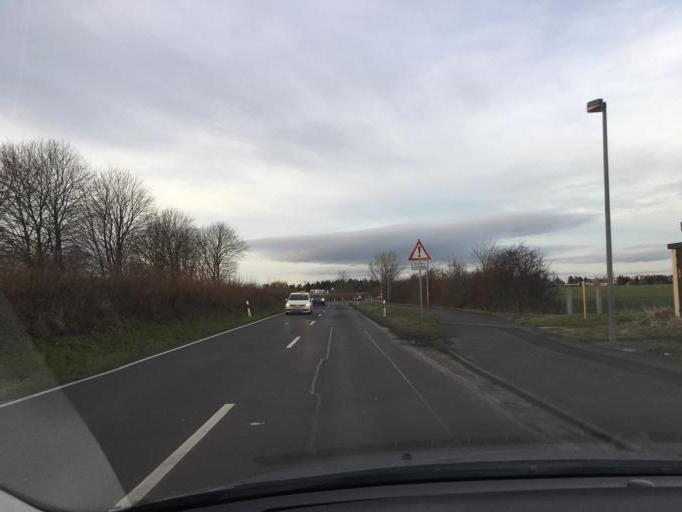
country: DE
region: Saxony
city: Grossposna
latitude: 51.2883
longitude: 12.4659
